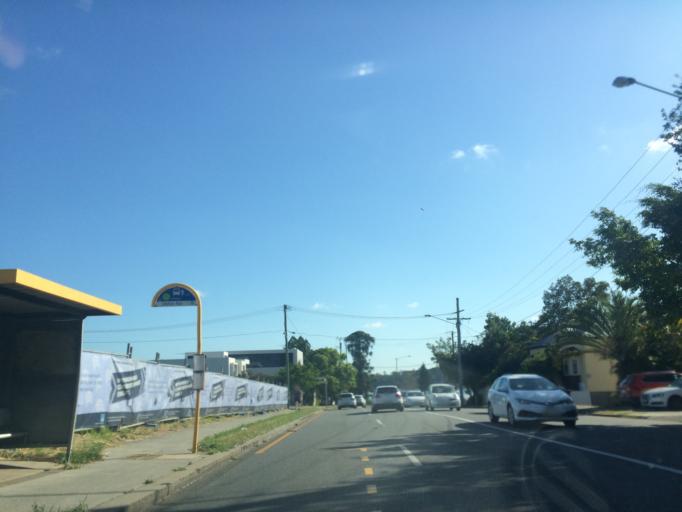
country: AU
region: Queensland
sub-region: Brisbane
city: Woolloongabba
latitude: -27.4775
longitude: 153.0485
